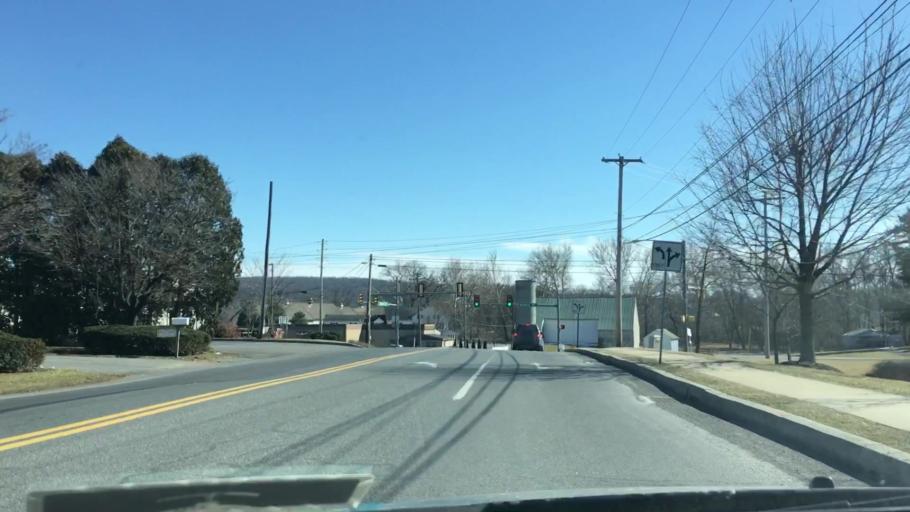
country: US
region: Pennsylvania
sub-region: Lancaster County
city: Reamstown
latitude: 40.2066
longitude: -76.1498
